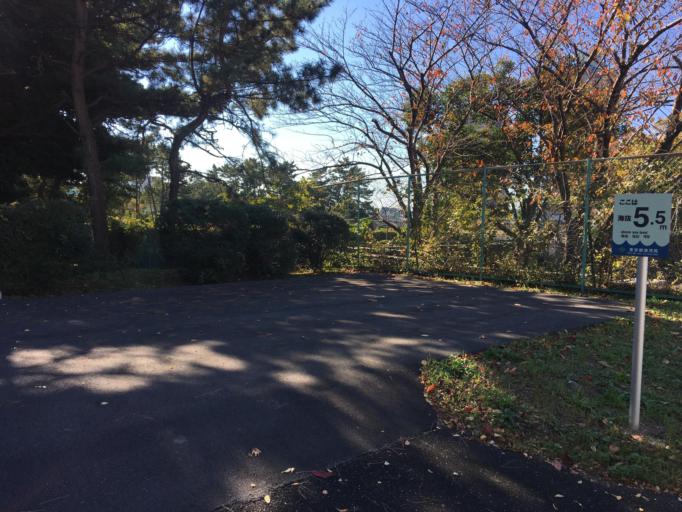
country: JP
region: Tokyo
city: Urayasu
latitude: 35.6459
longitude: 139.8097
